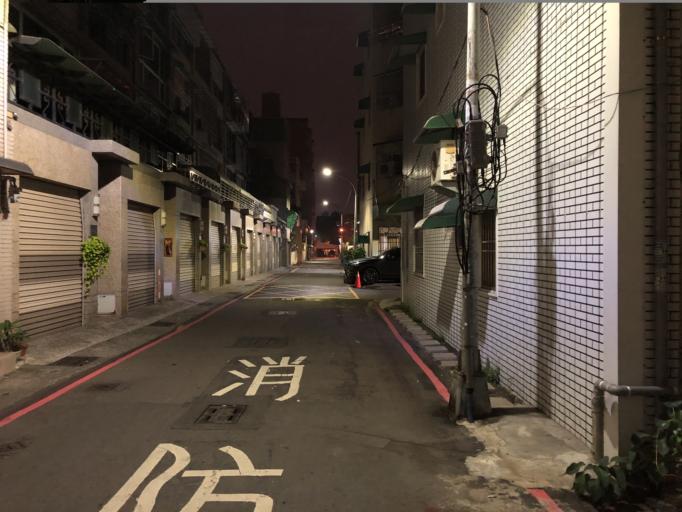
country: TW
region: Kaohsiung
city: Kaohsiung
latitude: 22.6383
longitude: 120.3267
